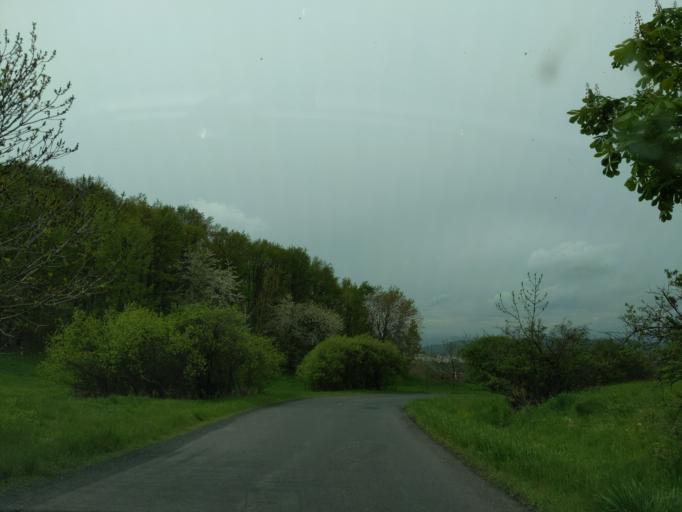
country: CZ
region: Ustecky
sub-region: Okres Usti nad Labem
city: Usti nad Labem
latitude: 50.6928
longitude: 14.0529
